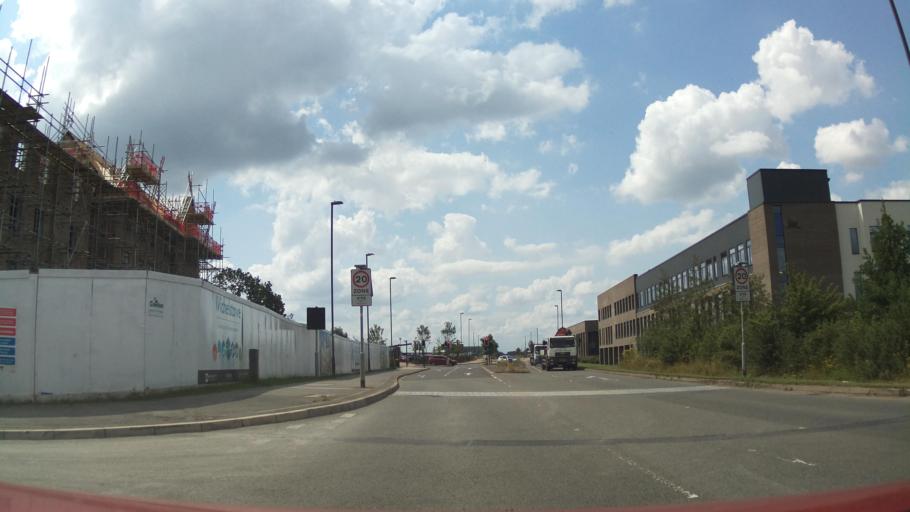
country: GB
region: England
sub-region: Borough of Swindon
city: Wroughton
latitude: 51.5464
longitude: -1.8072
